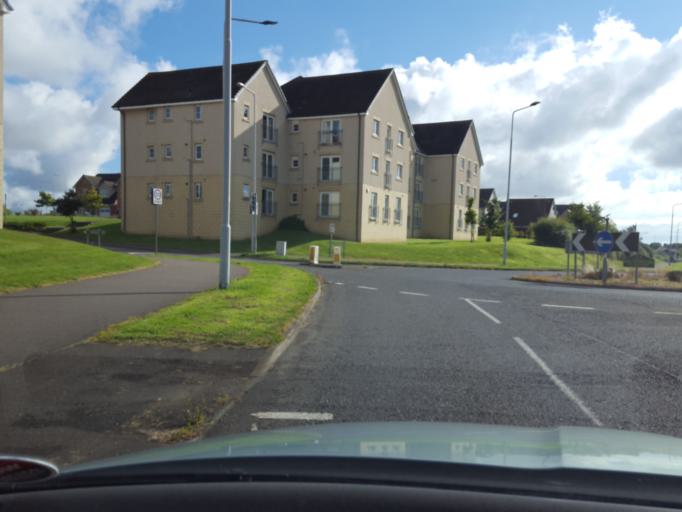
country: GB
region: Scotland
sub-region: Fife
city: Crossgates
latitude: 56.0580
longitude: -3.4045
